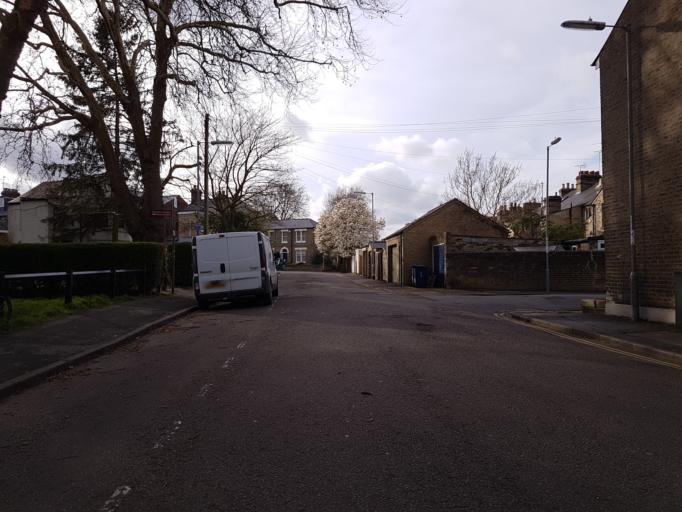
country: GB
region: England
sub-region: Cambridgeshire
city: Cambridge
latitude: 52.2143
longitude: 0.1181
